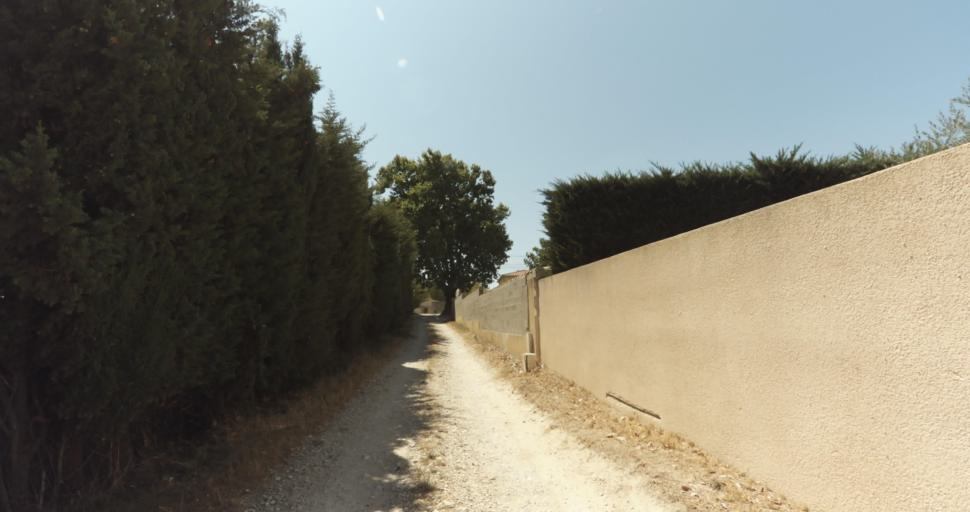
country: FR
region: Provence-Alpes-Cote d'Azur
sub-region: Departement du Vaucluse
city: Monteux
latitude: 44.0434
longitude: 4.9990
